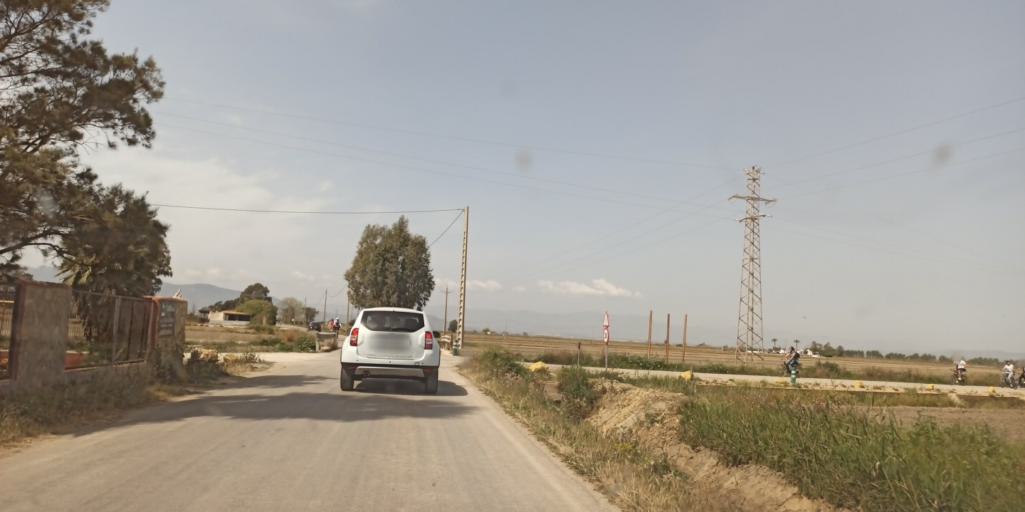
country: ES
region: Catalonia
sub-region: Provincia de Tarragona
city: Deltebre
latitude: 40.6460
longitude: 0.7177
